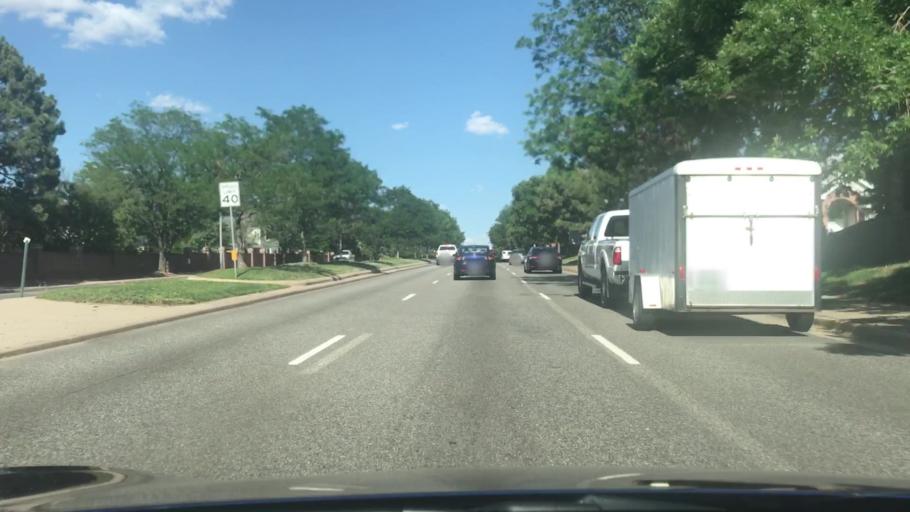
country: US
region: Colorado
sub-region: Arapahoe County
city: Dove Valley
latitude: 39.6530
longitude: -104.8274
